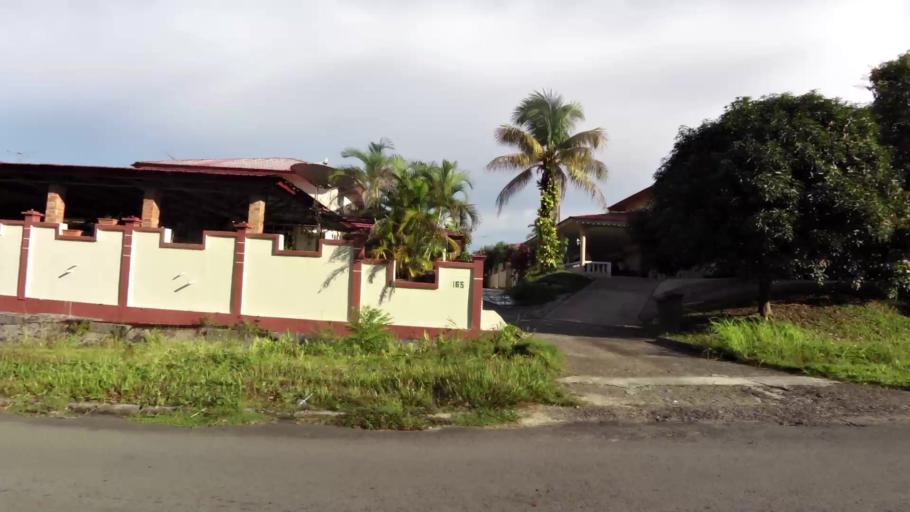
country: BN
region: Brunei and Muara
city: Bandar Seri Begawan
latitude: 4.9891
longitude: 114.9715
